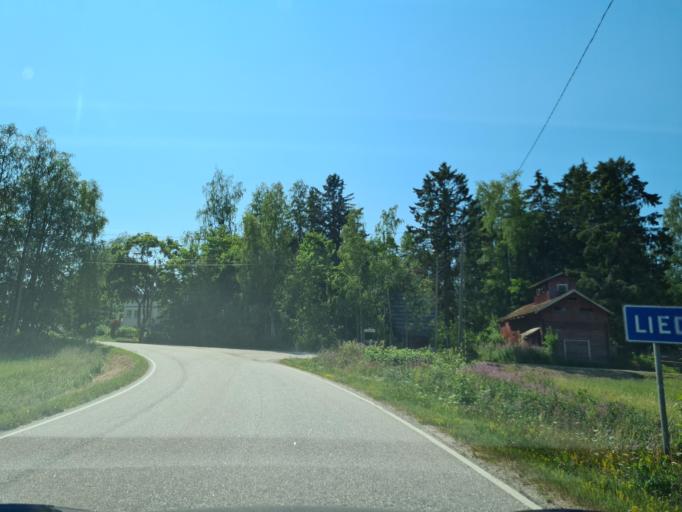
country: FI
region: Varsinais-Suomi
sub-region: Turku
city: Tarvasjoki
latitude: 60.5969
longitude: 22.6682
